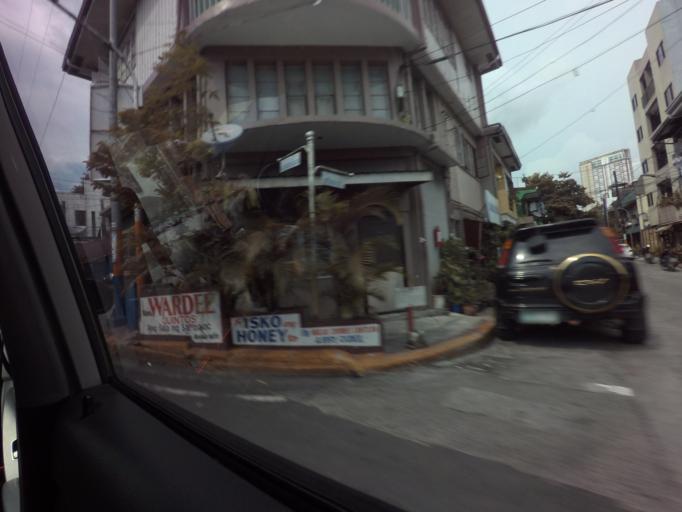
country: PH
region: Metro Manila
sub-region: City of Manila
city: Quiapo
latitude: 14.6032
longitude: 121.0082
